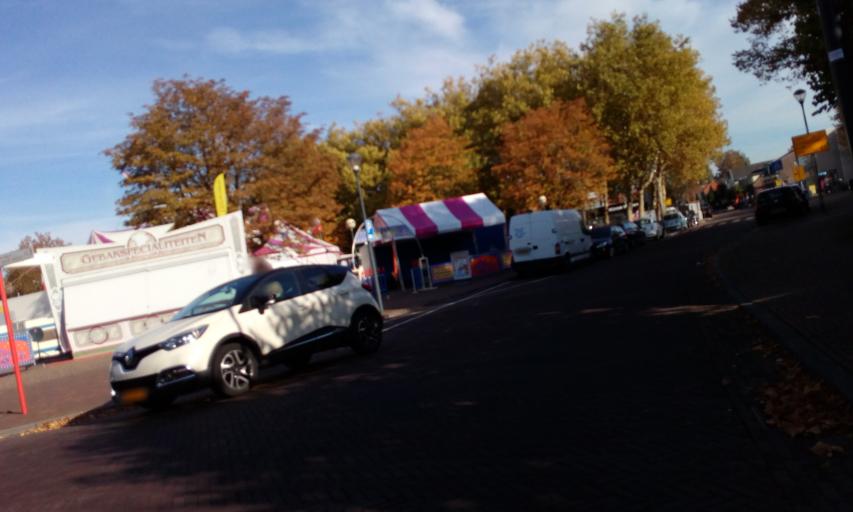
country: NL
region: Utrecht
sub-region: Stichtse Vecht
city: Spechtenkamp
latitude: 52.1065
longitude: 5.0114
